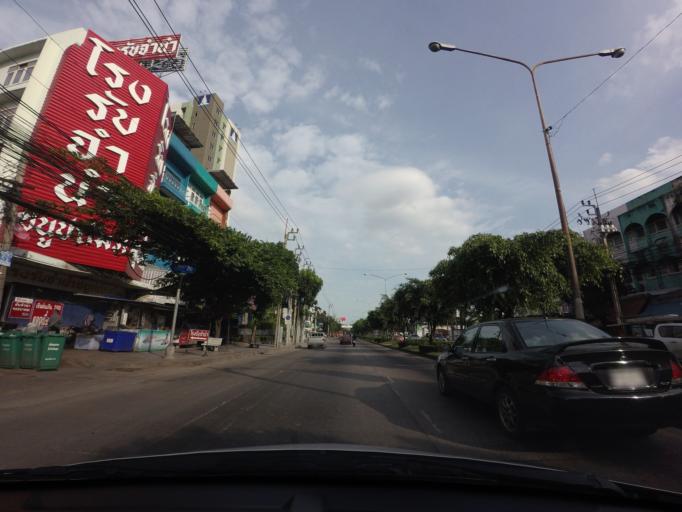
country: TH
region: Bangkok
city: Bueng Kum
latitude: 13.7944
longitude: 100.6517
